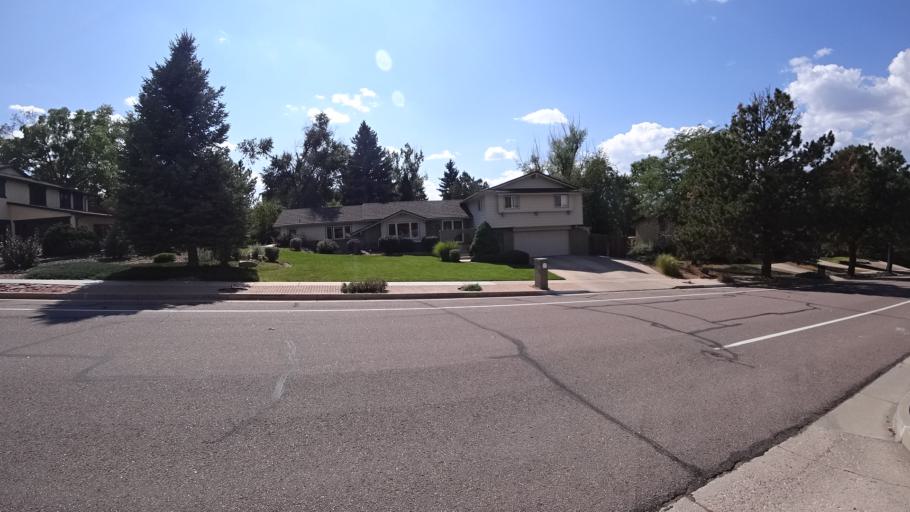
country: US
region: Colorado
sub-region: El Paso County
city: Cimarron Hills
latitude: 38.8724
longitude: -104.7431
